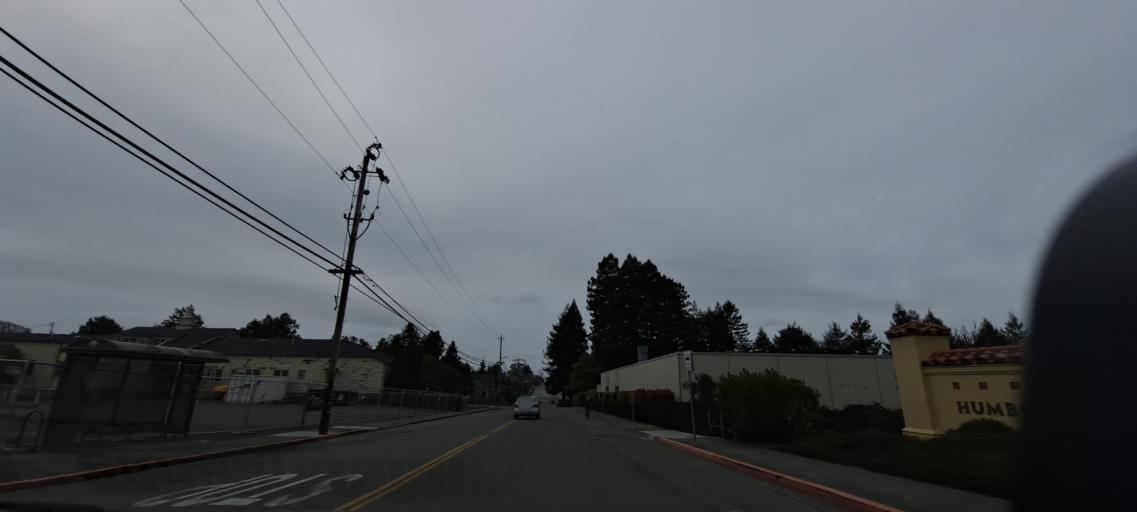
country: US
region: California
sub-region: Humboldt County
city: Arcata
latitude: 40.8717
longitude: -124.0791
